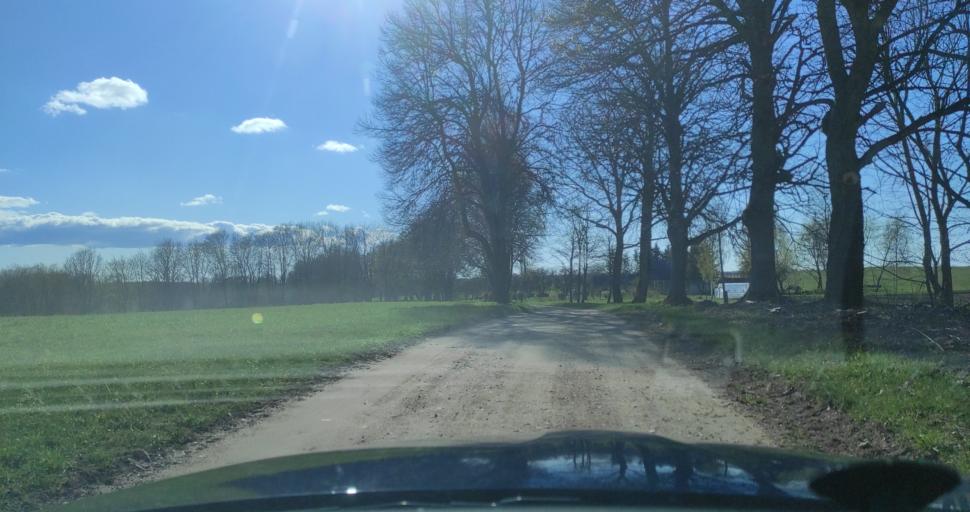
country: LV
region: Kuldigas Rajons
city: Kuldiga
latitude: 56.8694
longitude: 21.8491
